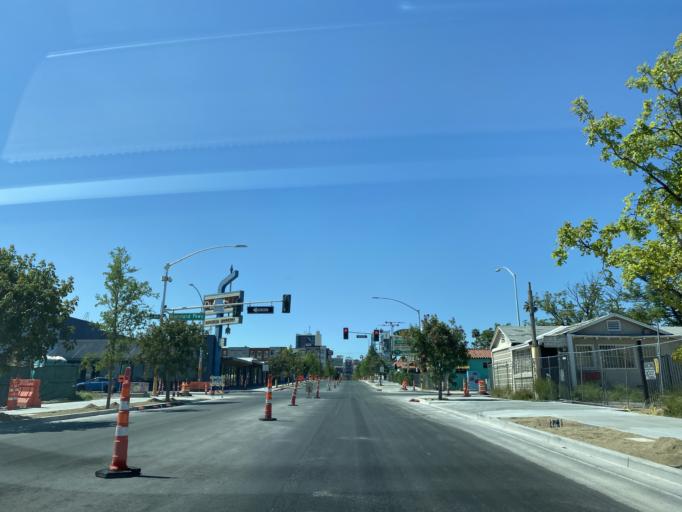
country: US
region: Nevada
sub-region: Clark County
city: Las Vegas
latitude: 36.1656
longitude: -115.1322
